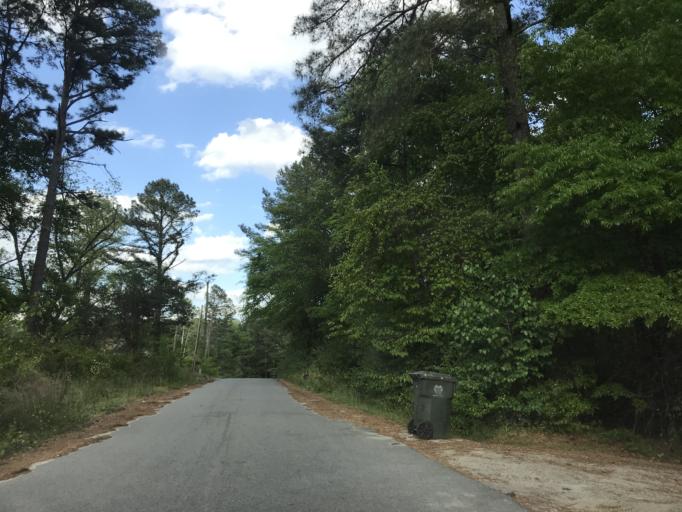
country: US
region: North Carolina
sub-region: Wake County
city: Raleigh
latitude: 35.7958
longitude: -78.5736
